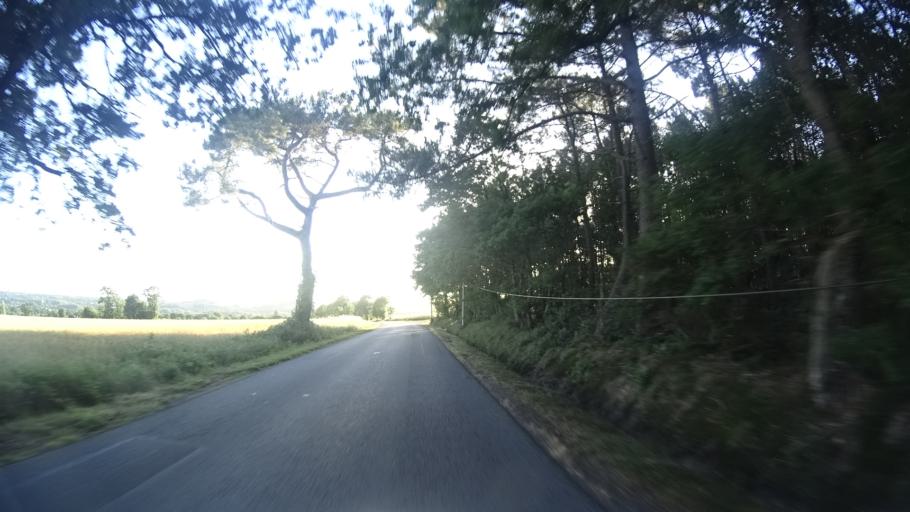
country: FR
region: Brittany
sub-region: Departement d'Ille-et-Vilaine
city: Langon
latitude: 47.7424
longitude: -1.8223
